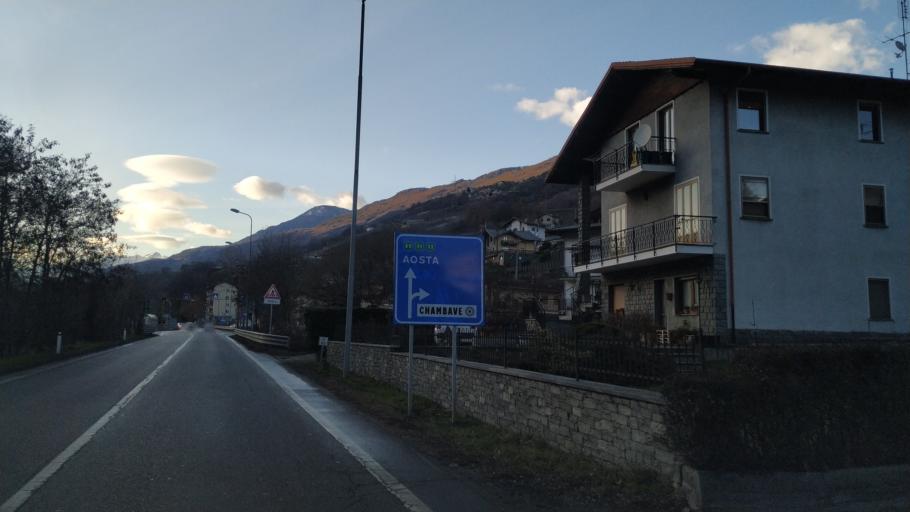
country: IT
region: Aosta Valley
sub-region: Valle d'Aosta
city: Chambave
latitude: 45.7434
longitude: 7.5469
